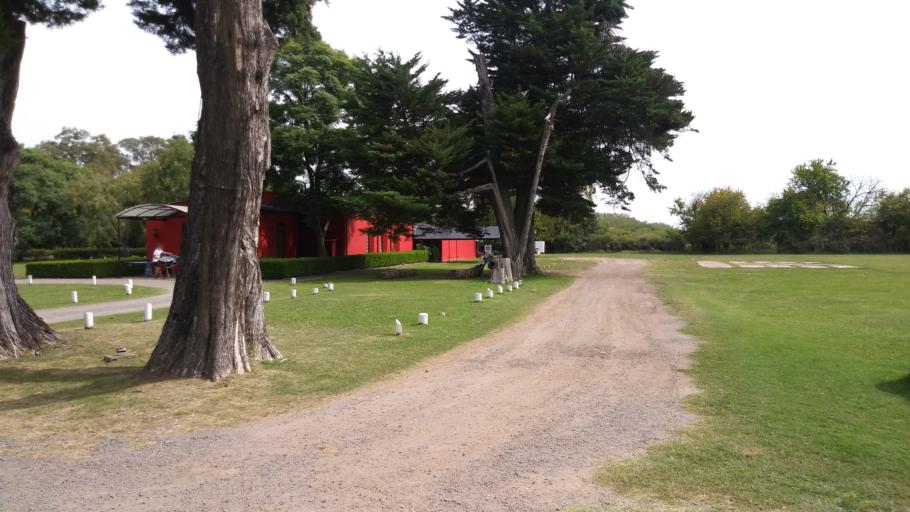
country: AR
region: Buenos Aires
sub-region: Partido de Lujan
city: Lujan
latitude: -34.5859
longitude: -59.1568
